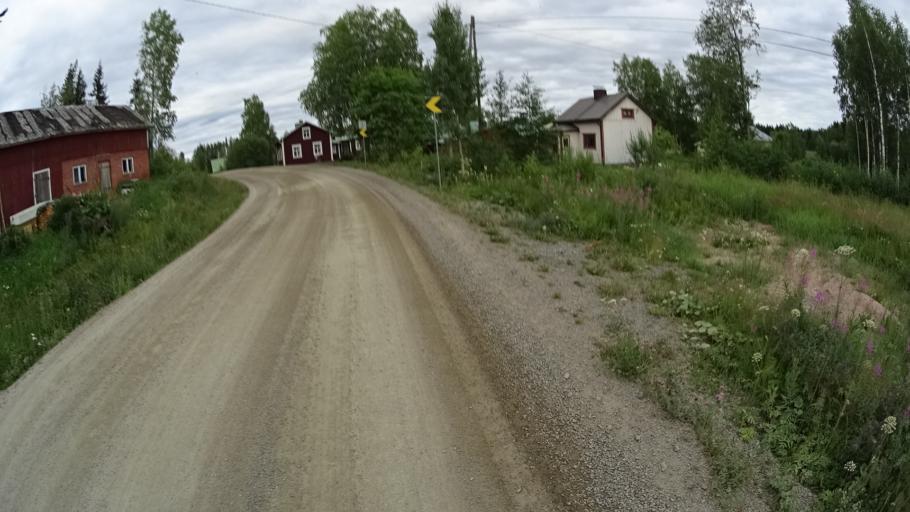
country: FI
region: Satakunta
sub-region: Pohjois-Satakunta
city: Jaemijaervi
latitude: 61.7670
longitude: 22.8401
